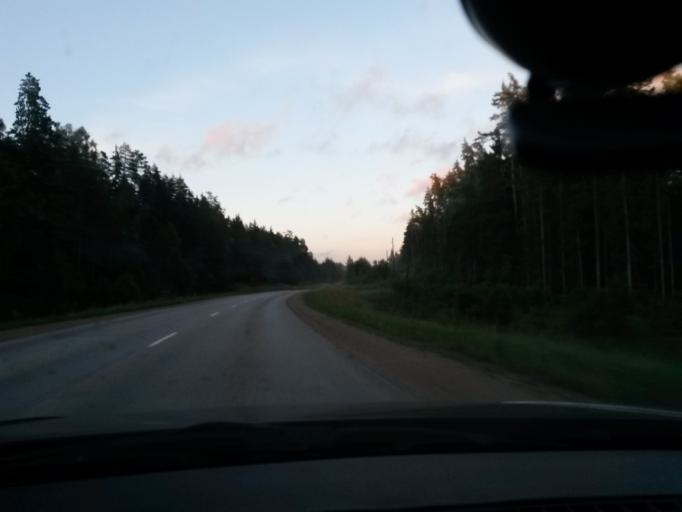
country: LV
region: Madonas Rajons
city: Madona
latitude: 56.8176
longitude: 26.1326
